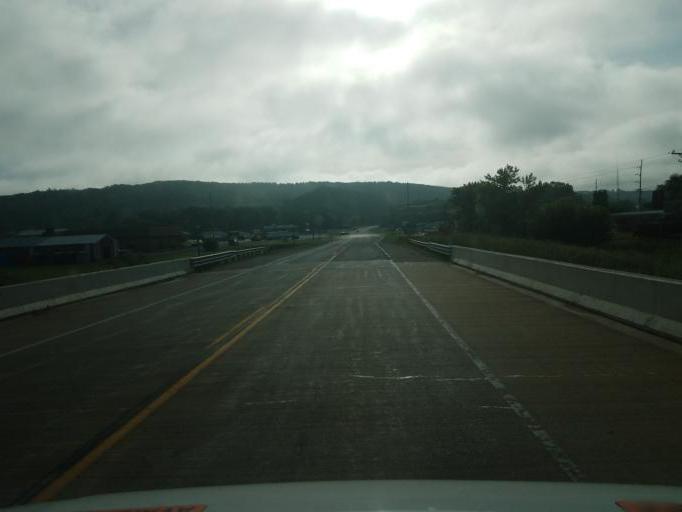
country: US
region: Wisconsin
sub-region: Juneau County
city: Elroy
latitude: 43.6807
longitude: -90.2684
